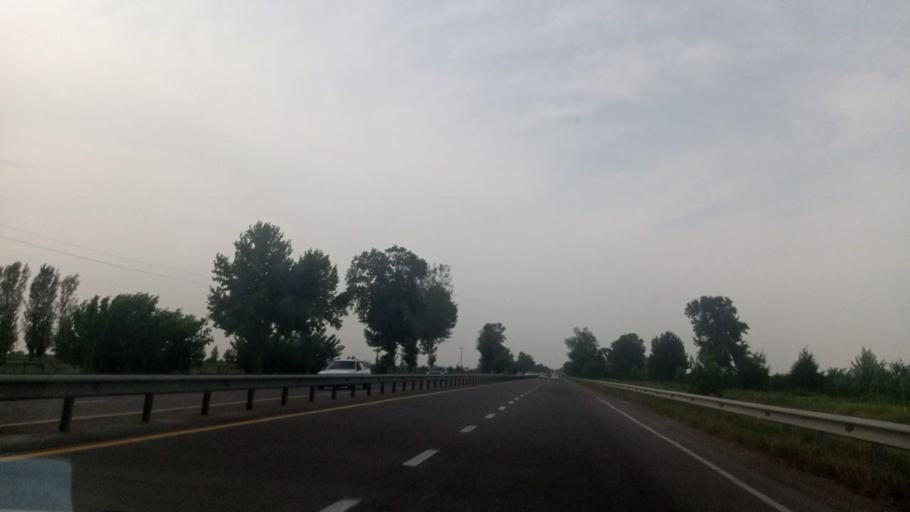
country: UZ
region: Toshkent Shahri
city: Bektemir
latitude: 41.1664
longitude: 69.4169
